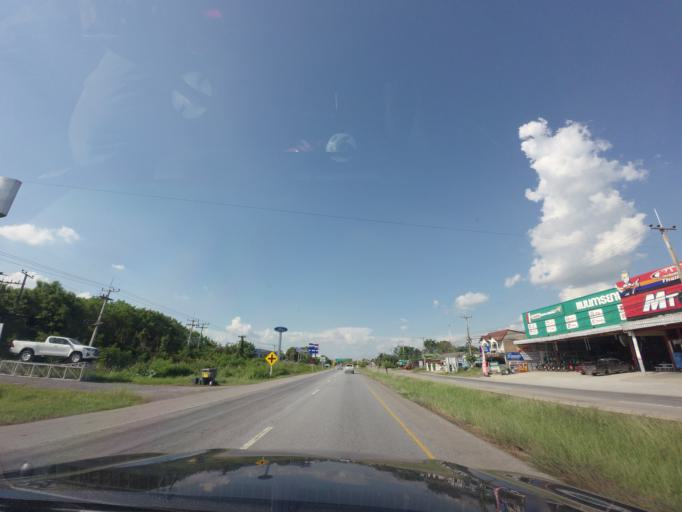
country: TH
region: Nakhon Ratchasima
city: Sida
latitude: 15.5428
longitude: 102.5469
